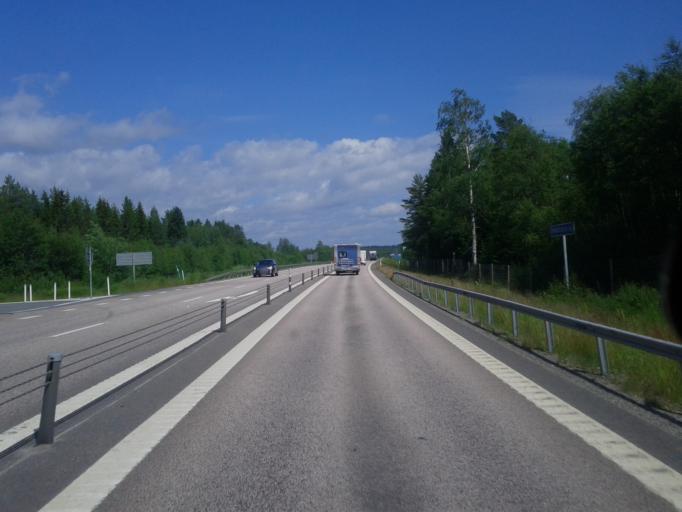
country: SE
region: Vaesterbotten
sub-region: Nordmalings Kommun
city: Nordmaling
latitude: 63.5662
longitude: 19.4315
